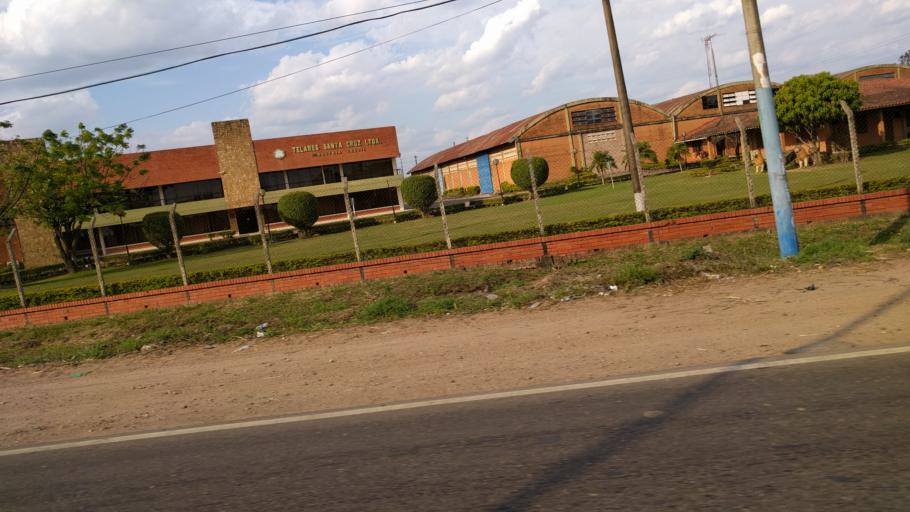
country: BO
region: Santa Cruz
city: Warnes
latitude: -17.5290
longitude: -63.1616
